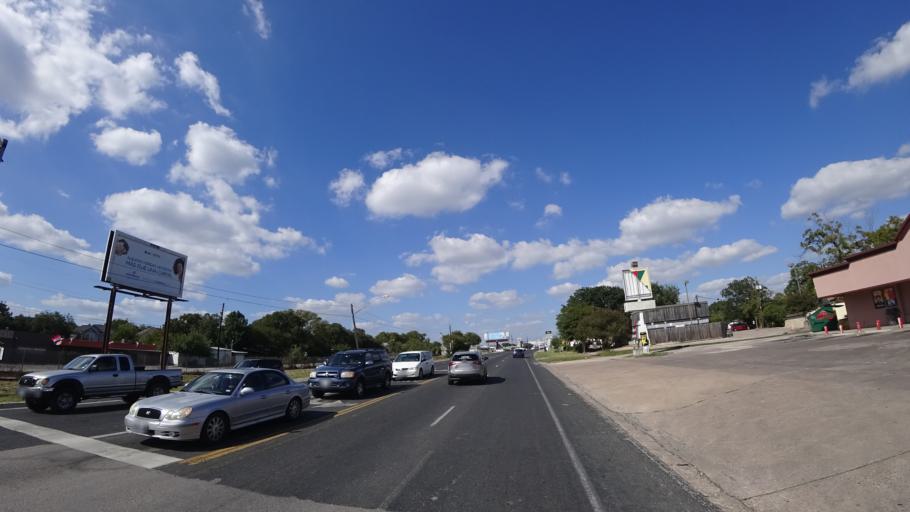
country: US
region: Texas
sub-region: Travis County
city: Austin
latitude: 30.3122
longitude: -97.7153
